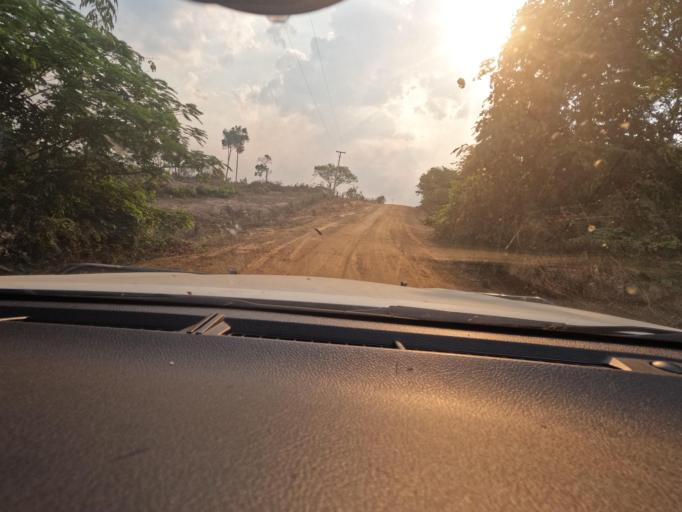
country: BR
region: Rondonia
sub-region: Porto Velho
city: Porto Velho
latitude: -8.6383
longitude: -63.1718
